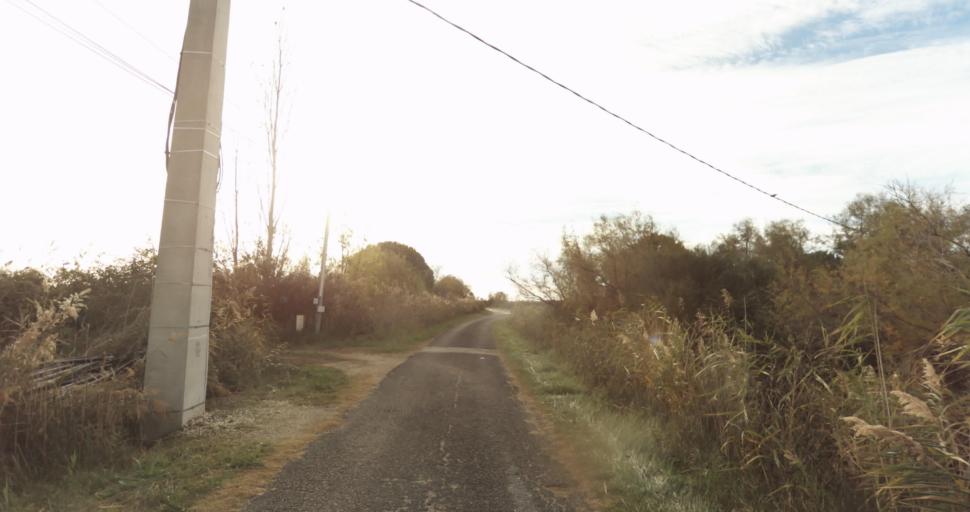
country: FR
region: Languedoc-Roussillon
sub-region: Departement du Gard
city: Aigues-Mortes
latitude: 43.5546
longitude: 4.2120
